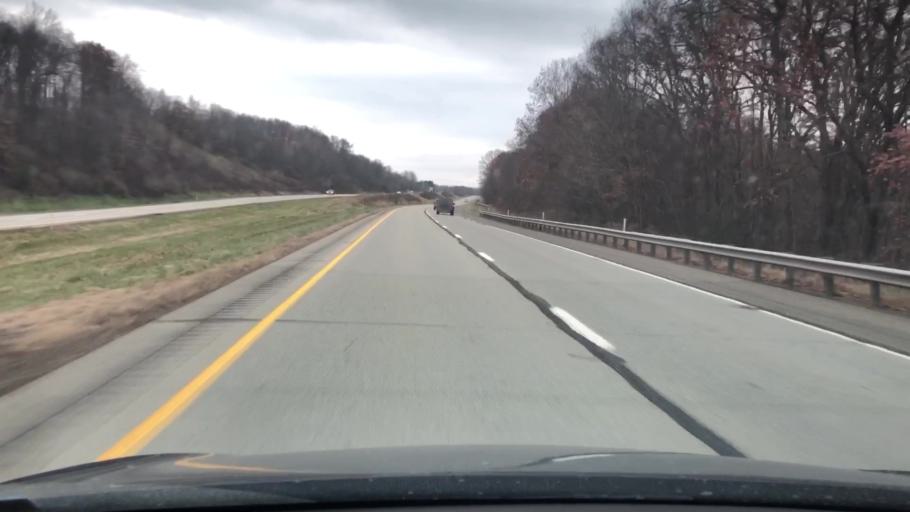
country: US
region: Pennsylvania
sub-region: Armstrong County
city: West Hills
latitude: 40.7957
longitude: -79.5725
